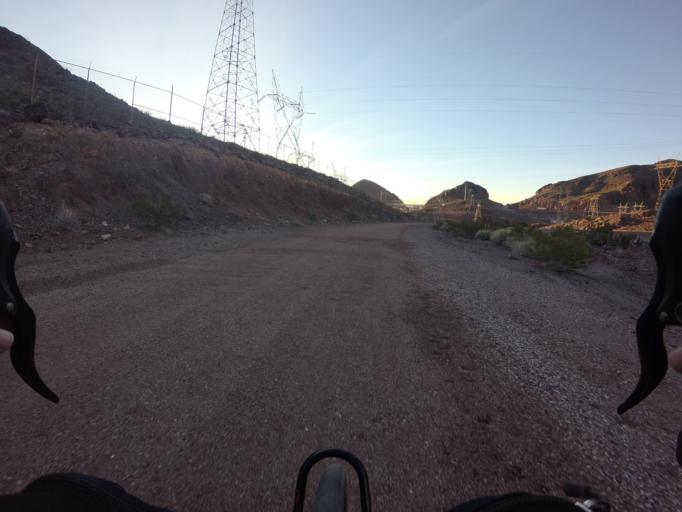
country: US
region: Nevada
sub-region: Clark County
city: Boulder City
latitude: 36.0194
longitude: -114.7454
